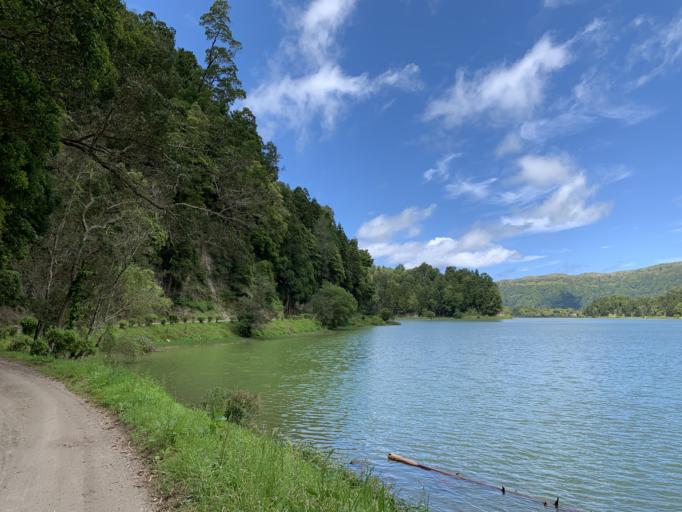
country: PT
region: Azores
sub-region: Ponta Delgada
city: Arrifes
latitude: 37.8451
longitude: -25.7938
